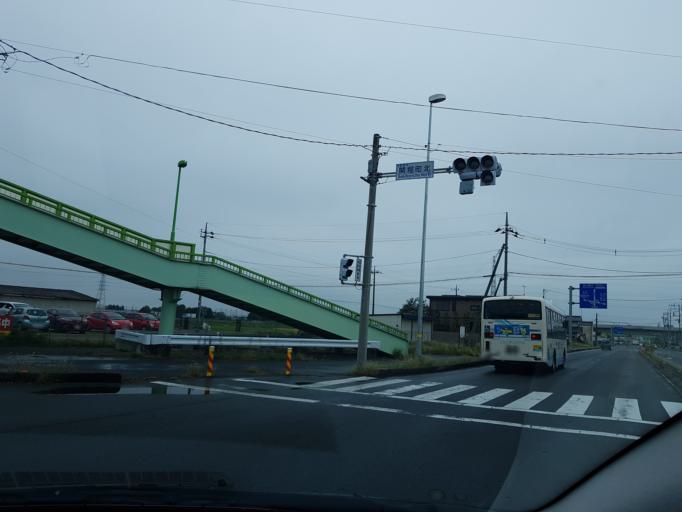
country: JP
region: Tochigi
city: Utsunomiya-shi
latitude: 36.5966
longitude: 139.8966
